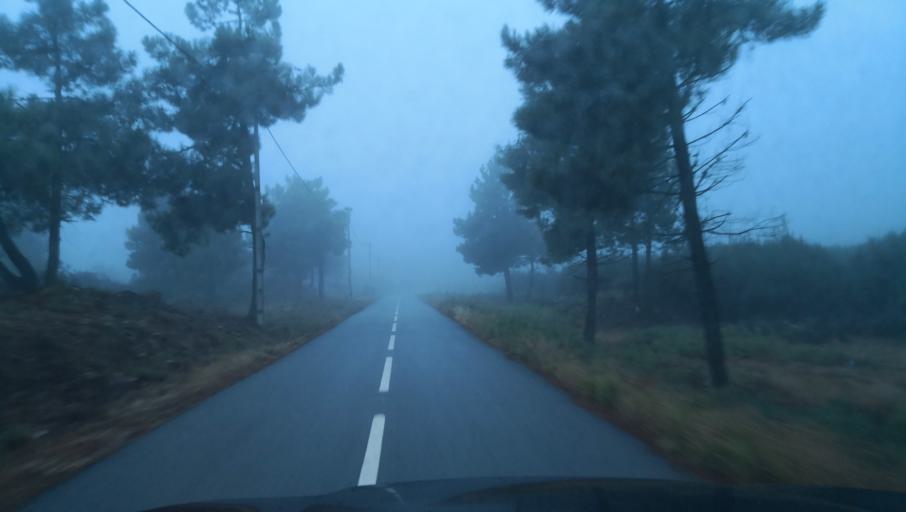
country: PT
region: Vila Real
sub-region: Sabrosa
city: Sabrosa
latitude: 41.2832
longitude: -7.5977
